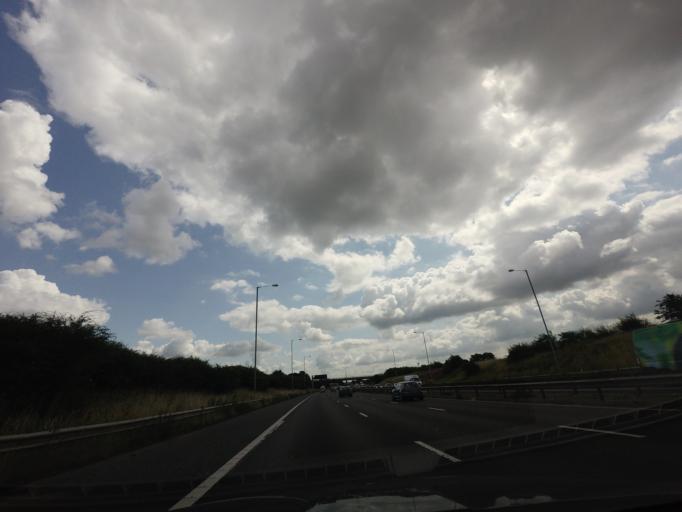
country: GB
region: England
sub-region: Borough of Wigan
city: Ashton in Makerfield
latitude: 53.5085
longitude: -2.6690
